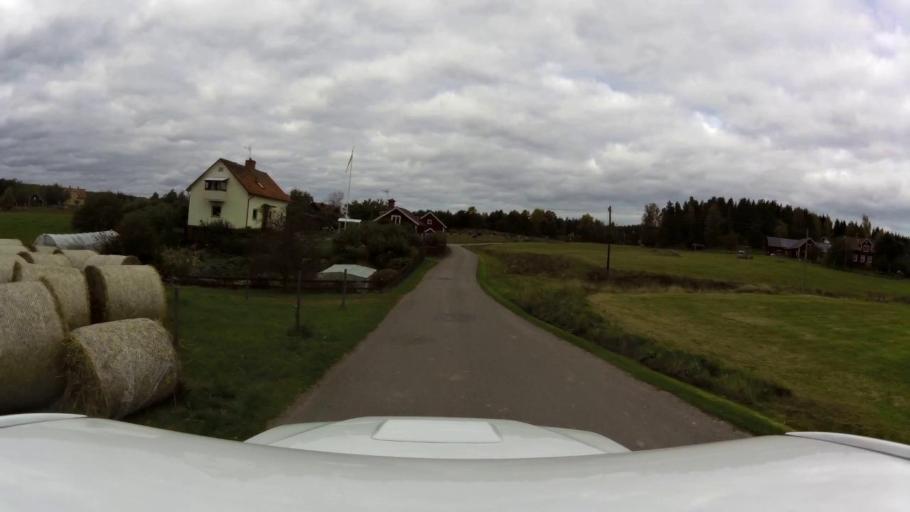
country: SE
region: OEstergoetland
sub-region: Kinda Kommun
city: Rimforsa
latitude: 58.1986
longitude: 15.5768
